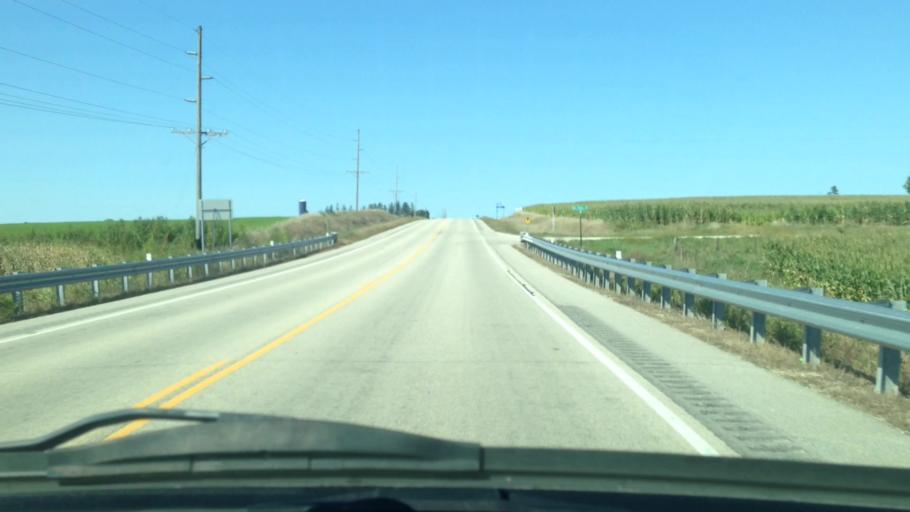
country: US
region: Minnesota
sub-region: Fillmore County
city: Rushford
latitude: 43.8893
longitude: -91.7398
